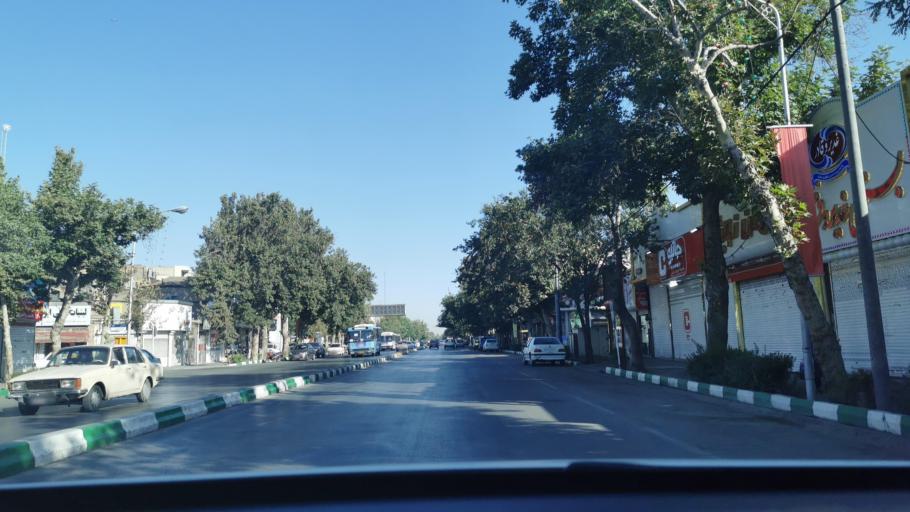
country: IR
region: Razavi Khorasan
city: Mashhad
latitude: 36.3091
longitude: 59.5941
